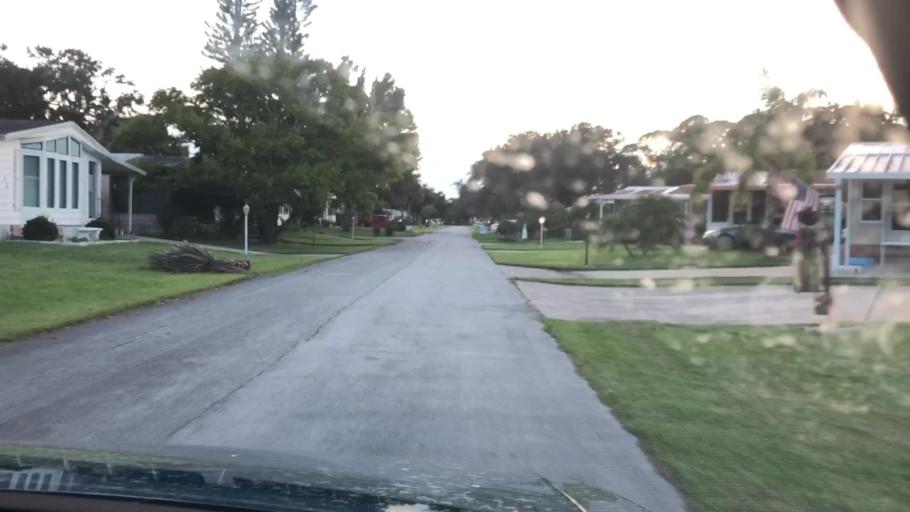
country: US
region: Florida
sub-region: Volusia County
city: Oak Hill
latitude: 28.9158
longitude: -80.8636
